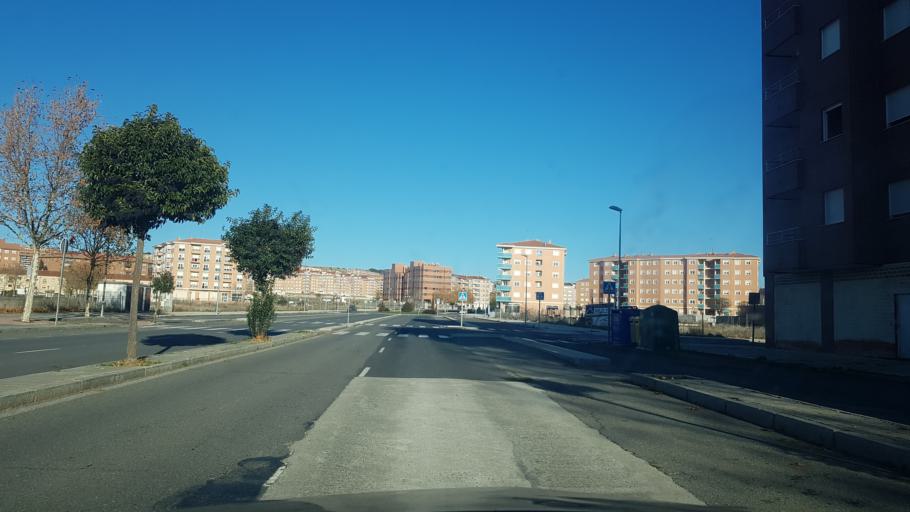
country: ES
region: Castille and Leon
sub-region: Provincia de Avila
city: Avila
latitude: 40.6432
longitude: -4.6858
